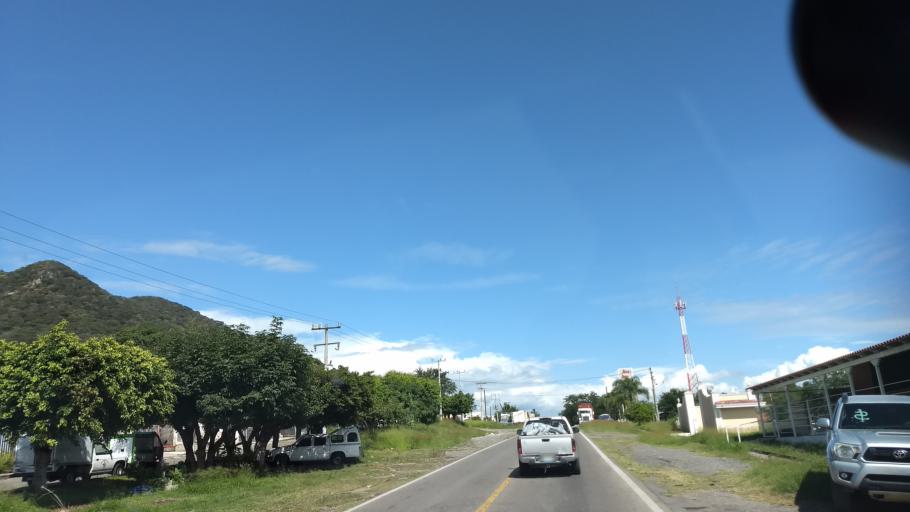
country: MX
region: Jalisco
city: Tuxpan
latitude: 19.5532
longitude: -103.3902
